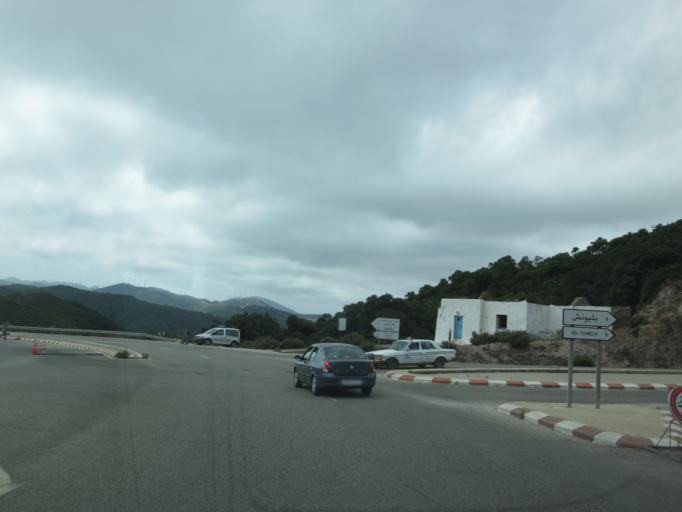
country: ES
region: Ceuta
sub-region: Ceuta
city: Ceuta
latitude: 35.8740
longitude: -5.4055
